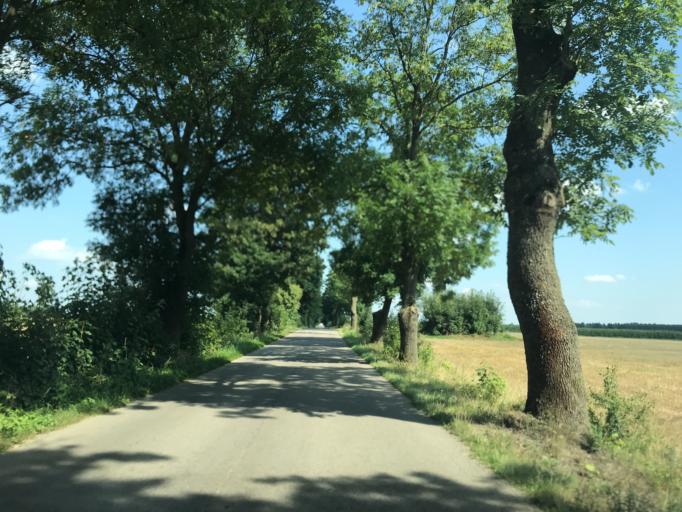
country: PL
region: Masovian Voivodeship
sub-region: Powiat zurominski
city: Lubowidz
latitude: 53.1742
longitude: 19.8745
